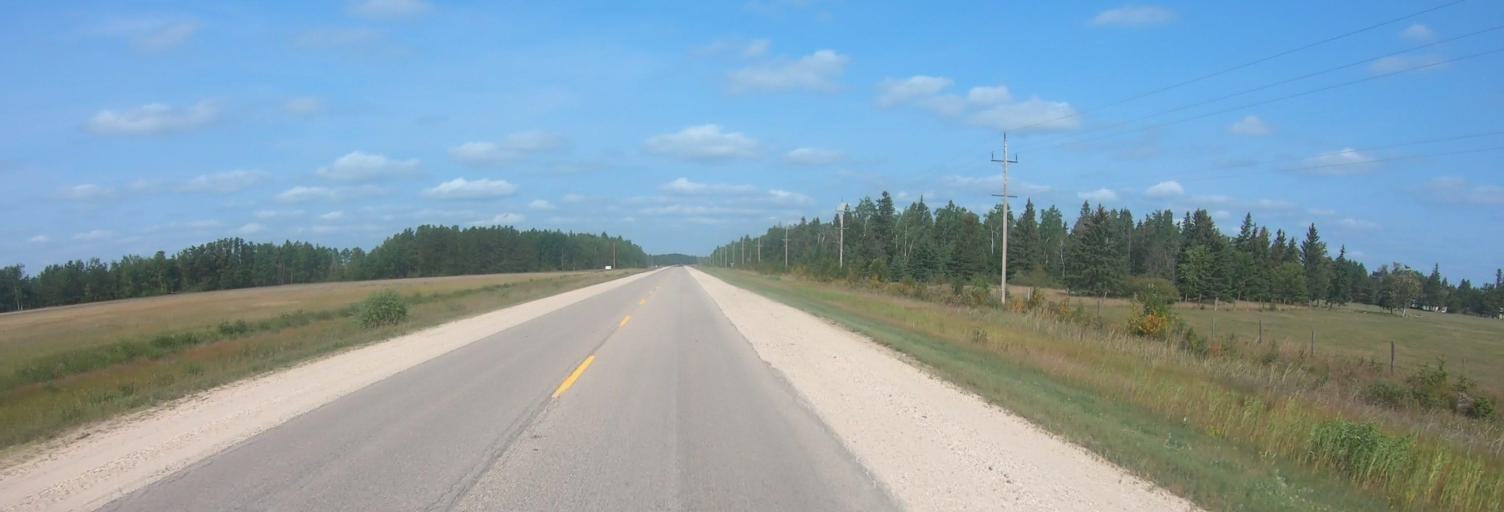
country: CA
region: Manitoba
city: La Broquerie
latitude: 49.1805
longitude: -96.2350
